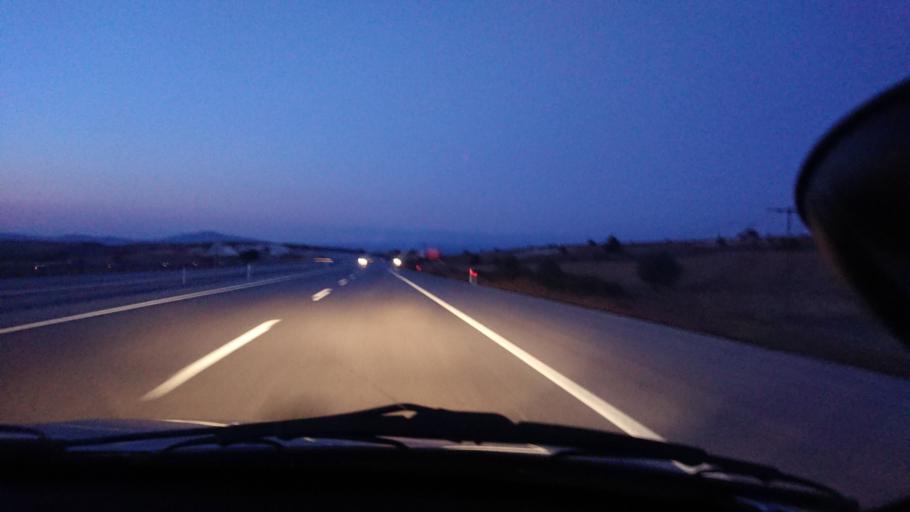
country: TR
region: Kuetahya
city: Cavdarhisar
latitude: 39.1641
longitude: 29.5935
